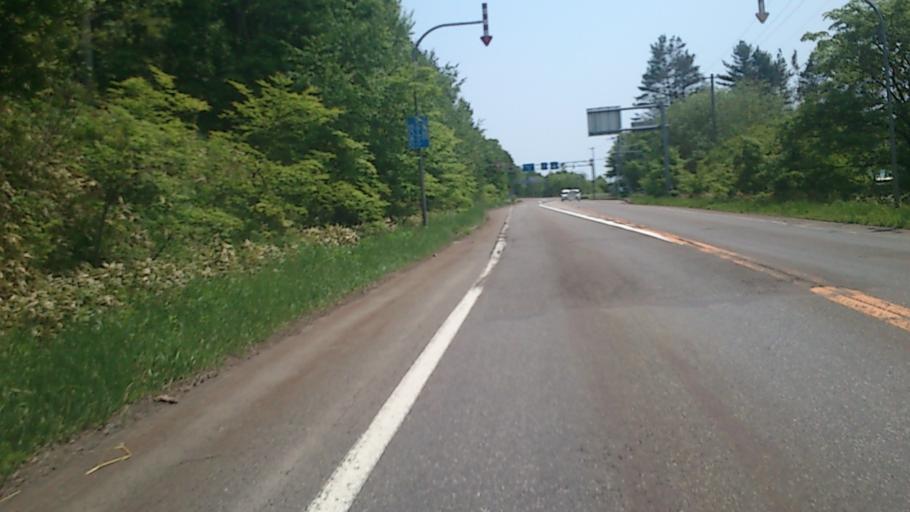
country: JP
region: Hokkaido
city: Otofuke
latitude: 43.2414
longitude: 143.4848
